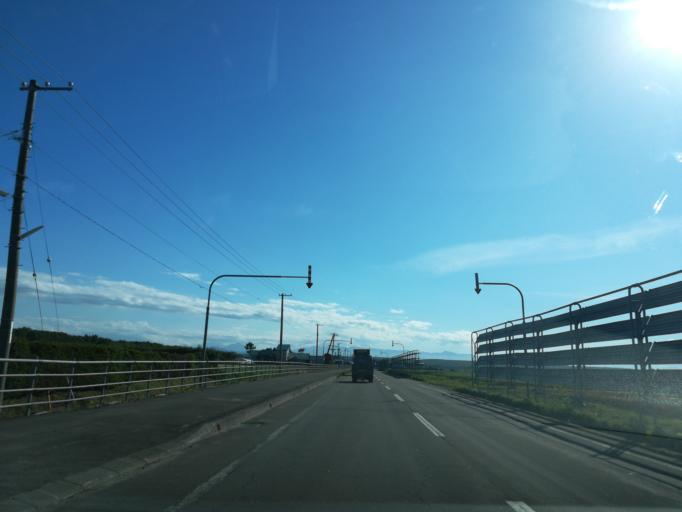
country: JP
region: Hokkaido
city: Kitahiroshima
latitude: 43.0437
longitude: 141.5903
